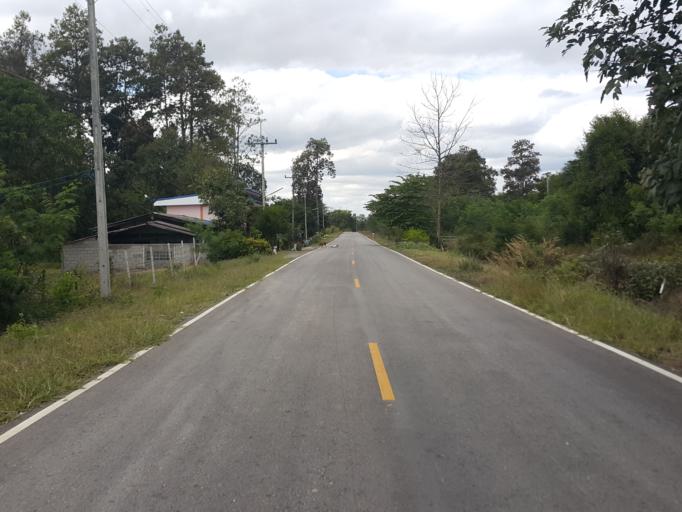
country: TH
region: Chiang Mai
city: San Kamphaeng
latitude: 18.8402
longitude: 99.1552
